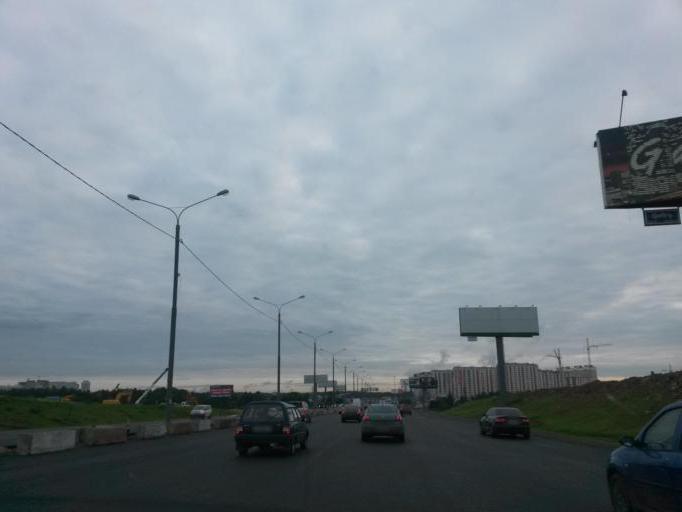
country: RU
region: Moskovskaya
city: Shcherbinka
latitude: 55.5230
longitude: 37.6095
